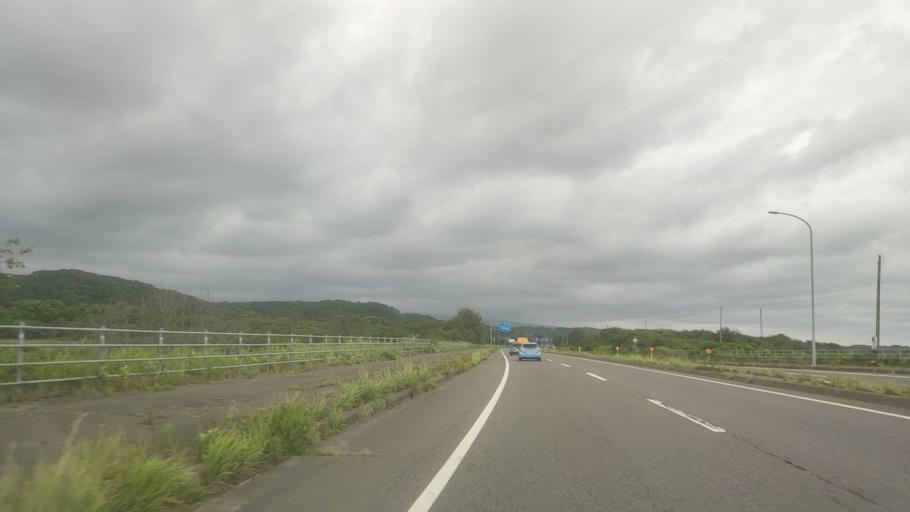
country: JP
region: Hokkaido
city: Shiraoi
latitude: 42.5594
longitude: 141.3804
